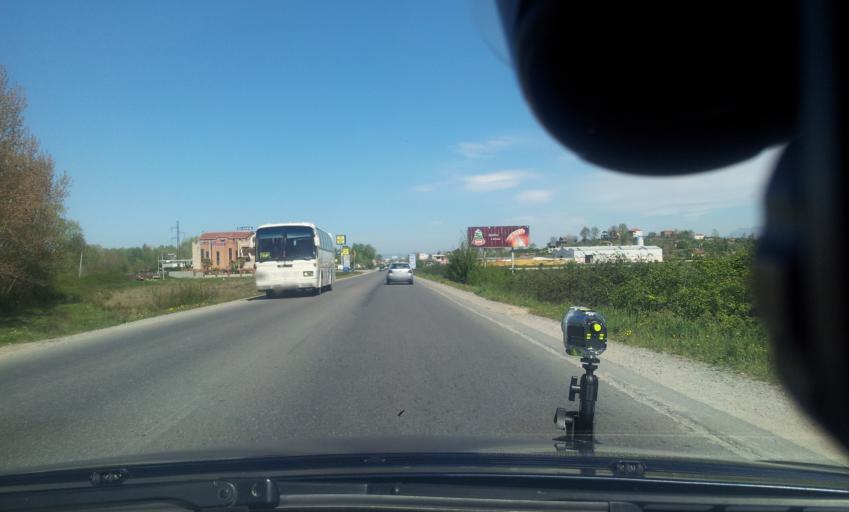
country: AL
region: Durres
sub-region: Rrethi i Krujes
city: Hasan
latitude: 41.5006
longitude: 19.6985
